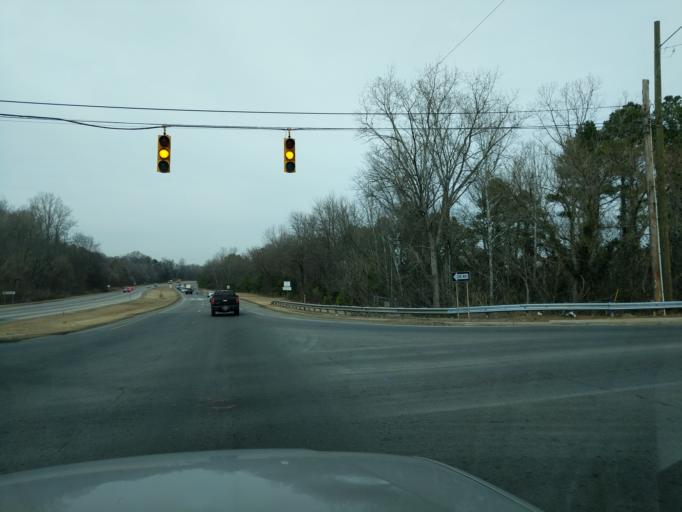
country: US
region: North Carolina
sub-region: Mecklenburg County
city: Charlotte
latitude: 35.2051
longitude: -80.9218
